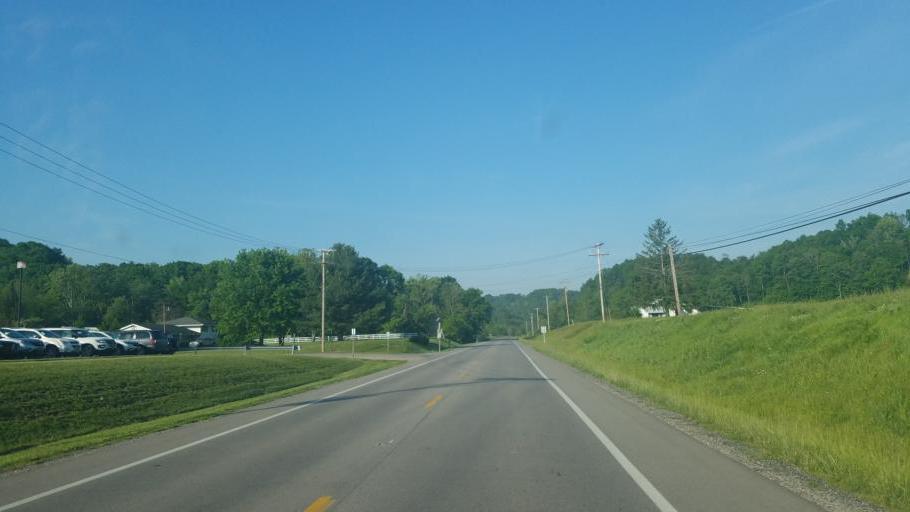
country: US
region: West Virginia
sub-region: Mason County
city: New Haven
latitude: 39.1218
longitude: -81.8846
